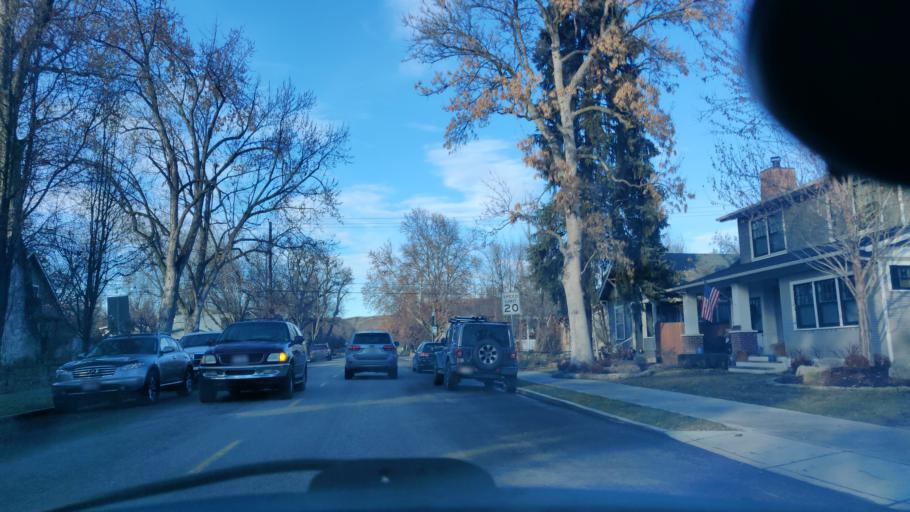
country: US
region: Idaho
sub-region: Ada County
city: Boise
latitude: 43.6314
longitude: -116.2034
